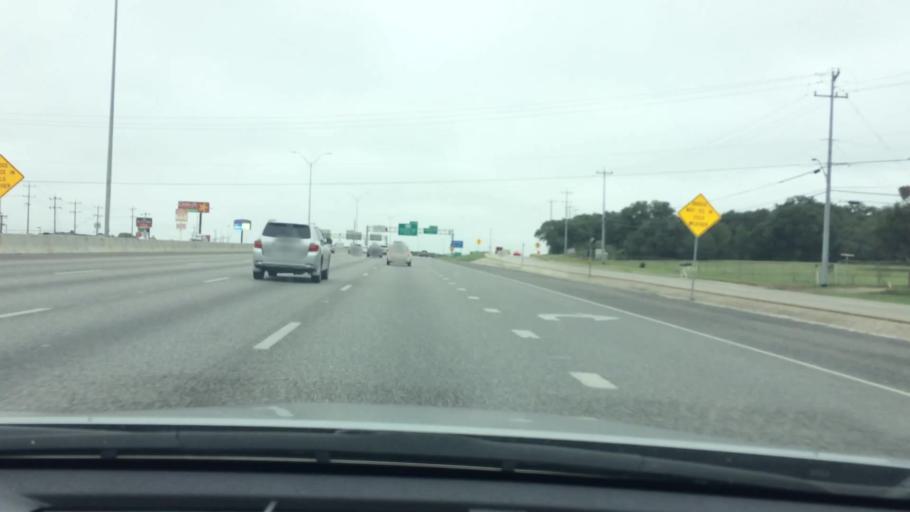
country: US
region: Texas
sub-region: Bexar County
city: Live Oak
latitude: 29.5578
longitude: -98.3454
